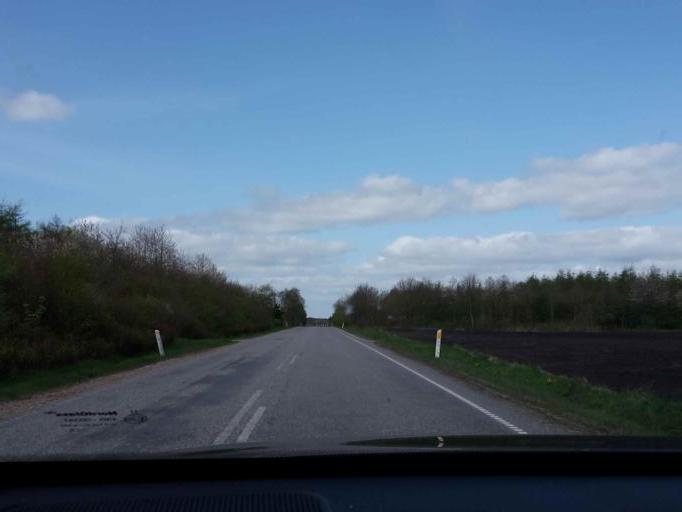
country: DK
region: South Denmark
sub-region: Billund Kommune
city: Grindsted
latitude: 55.7006
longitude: 8.8235
